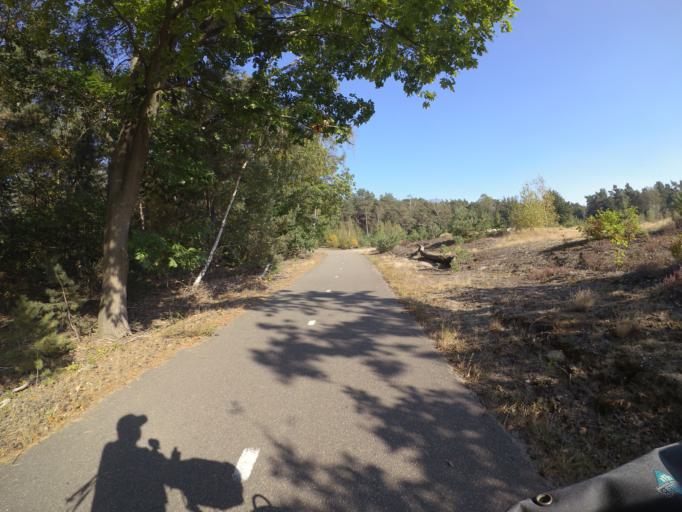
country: NL
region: North Brabant
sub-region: Gemeente Oirschot
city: Oostelbeers
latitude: 51.4674
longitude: 5.2989
